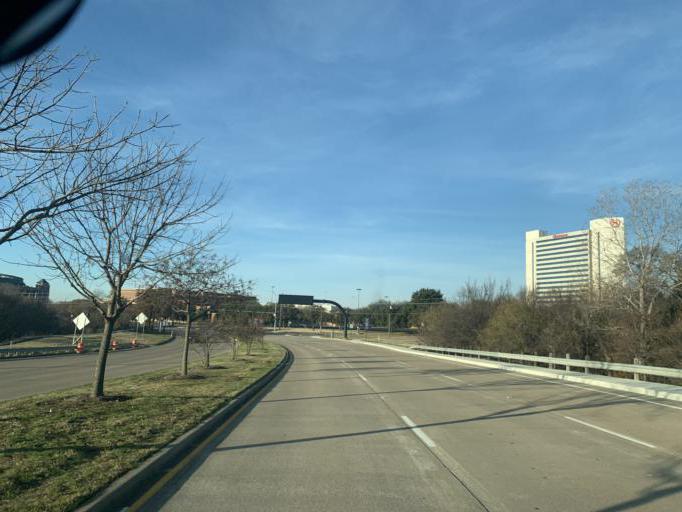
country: US
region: Texas
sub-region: Tarrant County
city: Arlington
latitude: 32.7568
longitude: -97.0785
